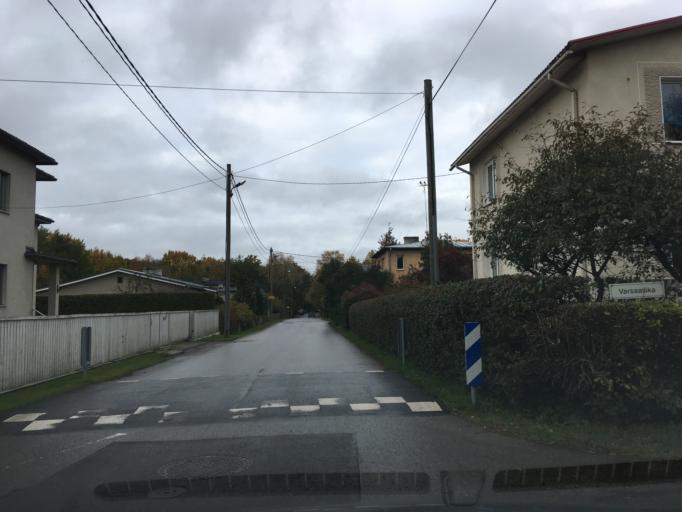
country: EE
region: Harju
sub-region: Tallinna linn
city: Kose
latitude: 59.4554
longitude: 24.8511
